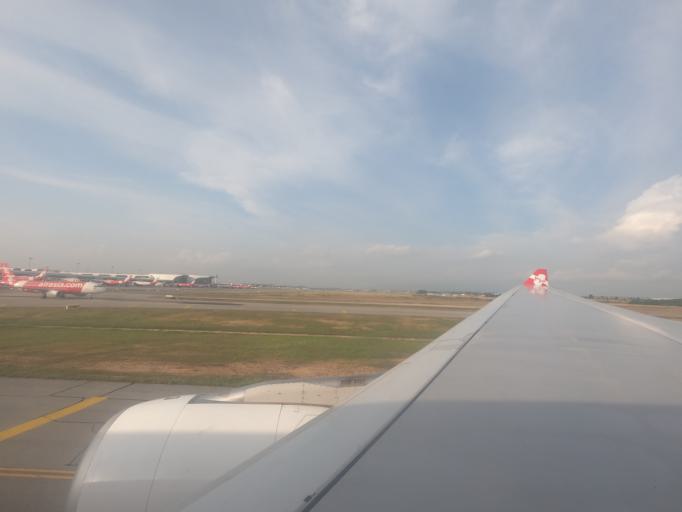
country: MY
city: Sungai Pelek New Village
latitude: 2.7317
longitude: 101.6839
